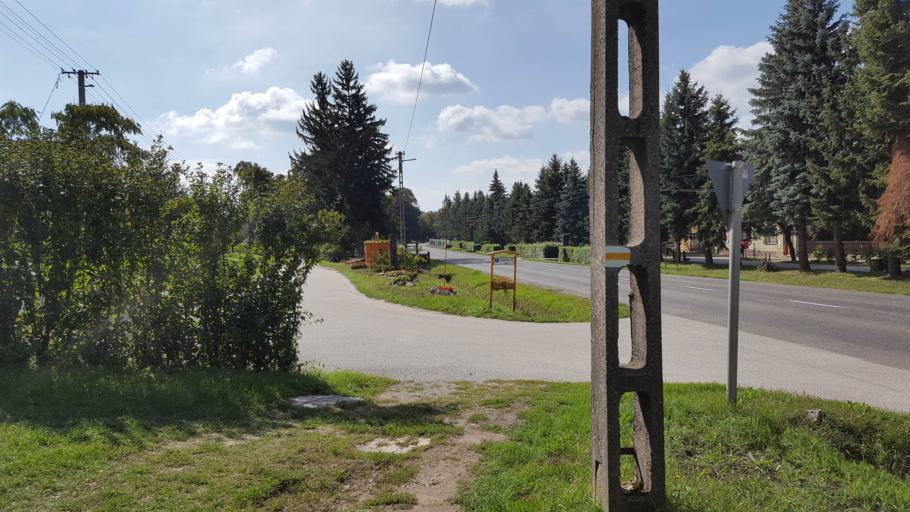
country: HU
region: Somogy
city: Marcali
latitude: 46.5011
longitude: 17.4239
